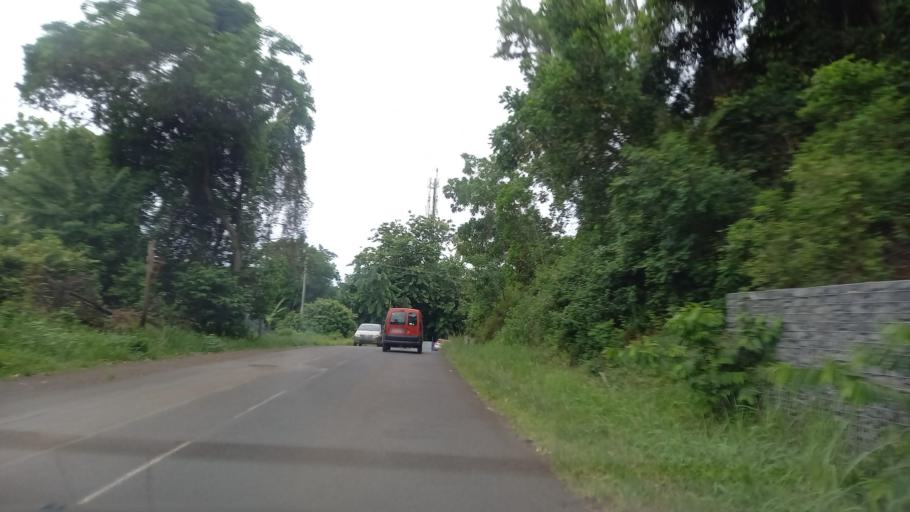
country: YT
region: Sada
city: Sada
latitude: -12.8526
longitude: 45.1048
